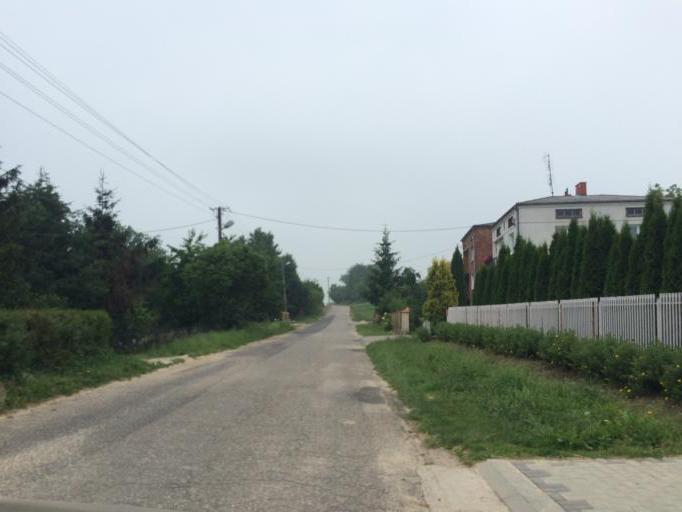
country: PL
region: Lublin Voivodeship
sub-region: Powiat pulawski
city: Markuszow
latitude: 51.3596
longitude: 22.2671
